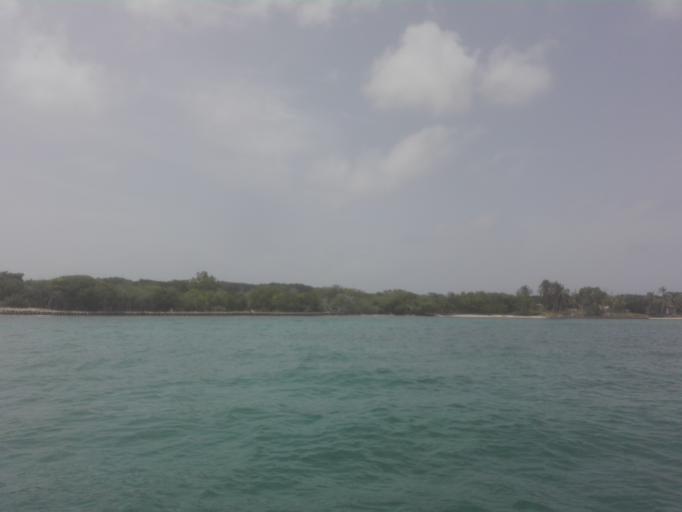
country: CO
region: Bolivar
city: Turbana
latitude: 10.1584
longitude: -75.6859
